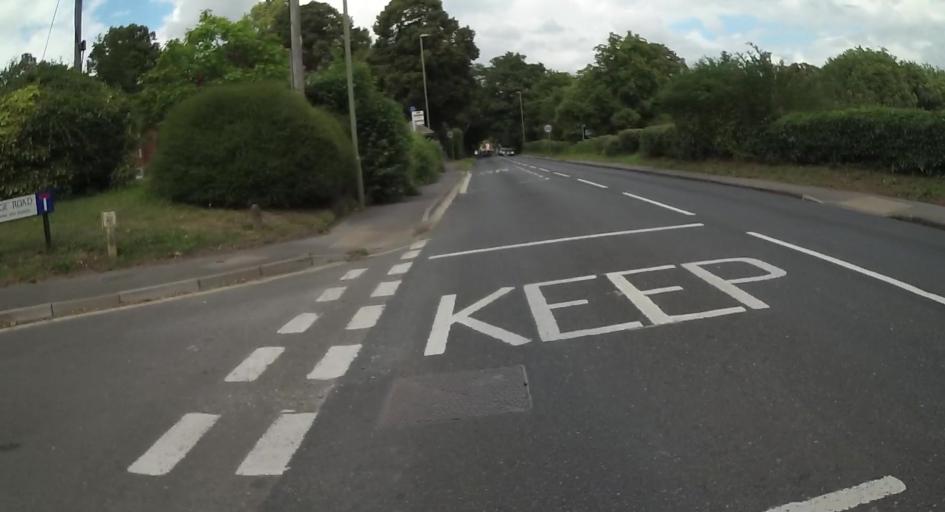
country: GB
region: England
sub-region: Hampshire
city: Winchester
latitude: 51.0447
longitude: -1.3249
